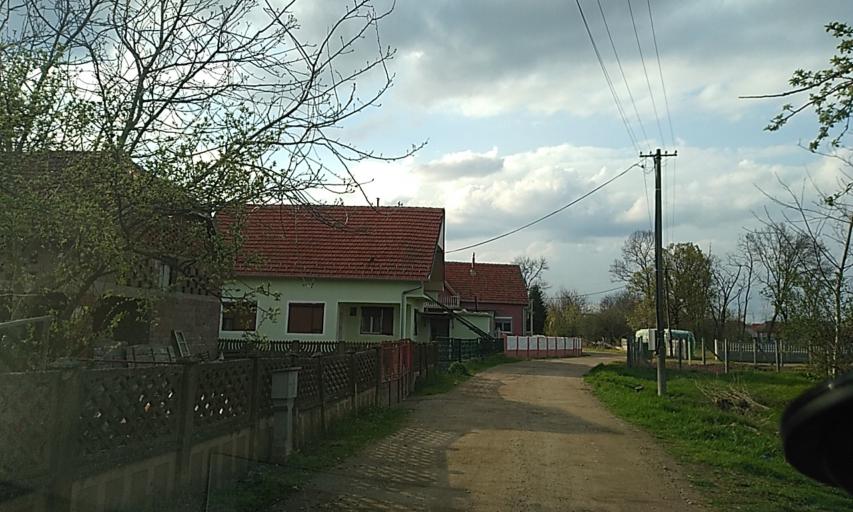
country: RS
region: Central Serbia
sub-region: Nisavski Okrug
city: Razanj
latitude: 43.5928
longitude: 21.6099
